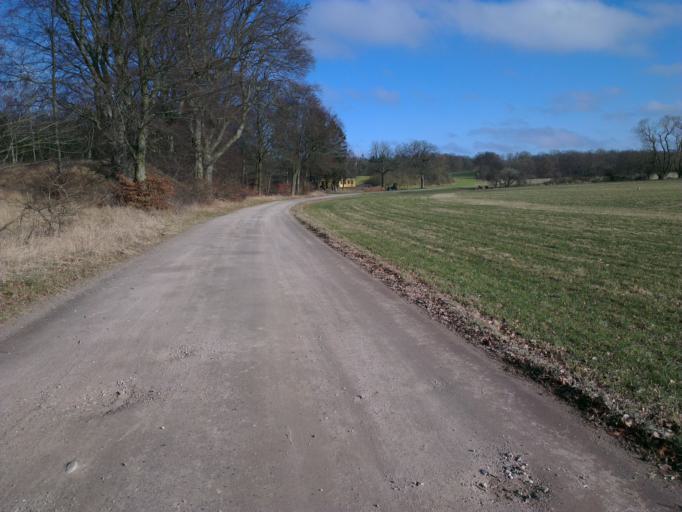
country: DK
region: Capital Region
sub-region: Frederikssund Kommune
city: Jaegerspris
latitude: 55.8873
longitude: 12.0039
